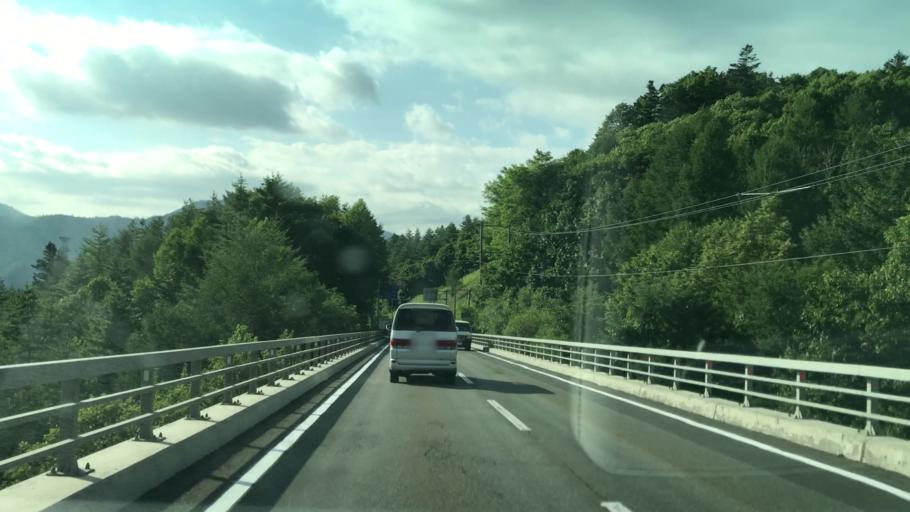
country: JP
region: Hokkaido
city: Shimo-furano
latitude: 42.8877
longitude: 142.2009
